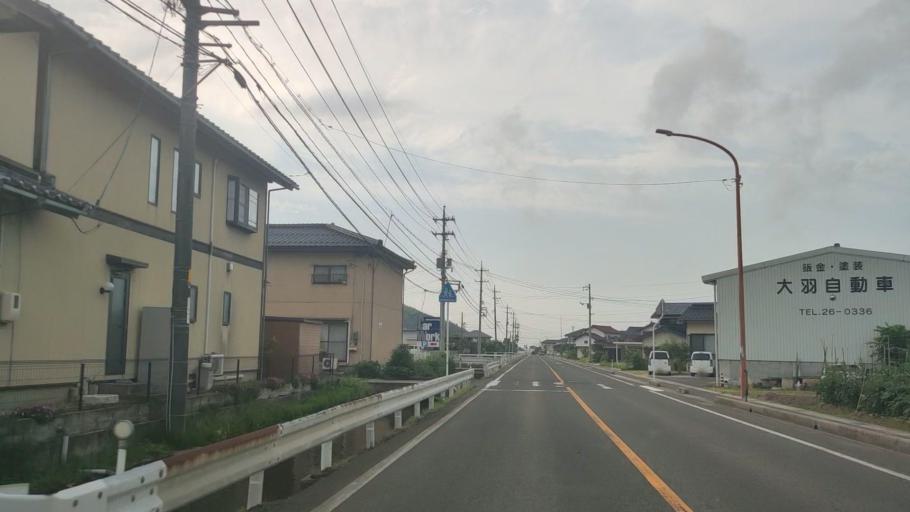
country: JP
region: Tottori
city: Kurayoshi
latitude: 35.4609
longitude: 133.8347
